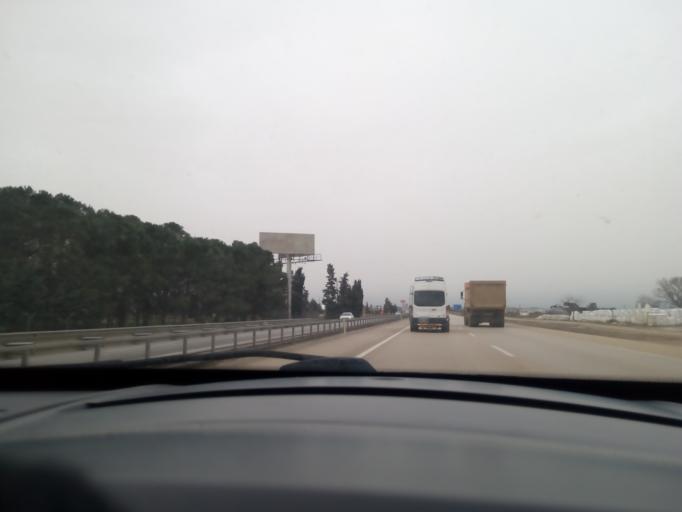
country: TR
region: Bursa
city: Tatkavakli
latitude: 40.0316
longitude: 28.3476
